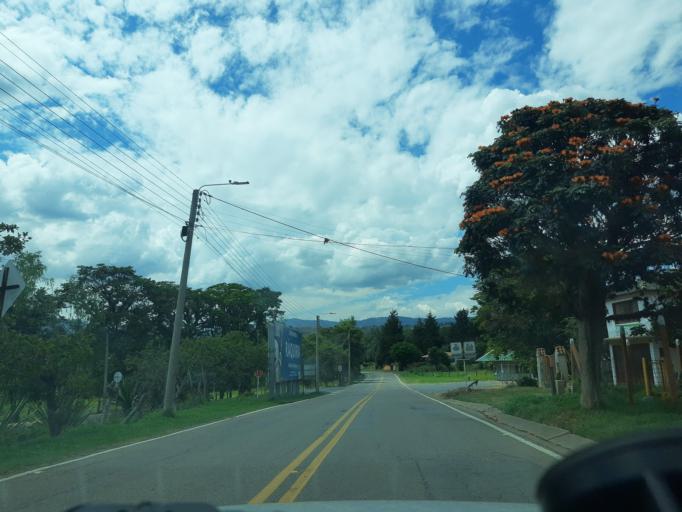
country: CO
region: Boyaca
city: Raquira
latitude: 5.5719
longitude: -73.6526
